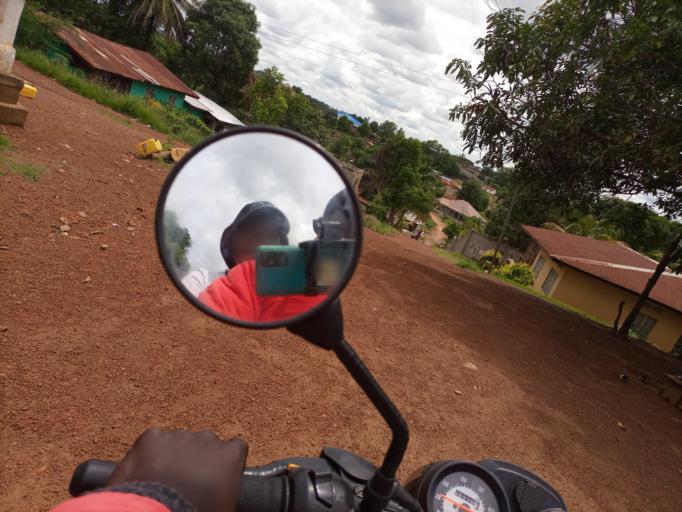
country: SL
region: Southern Province
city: Bo
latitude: 7.9694
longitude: -11.7172
